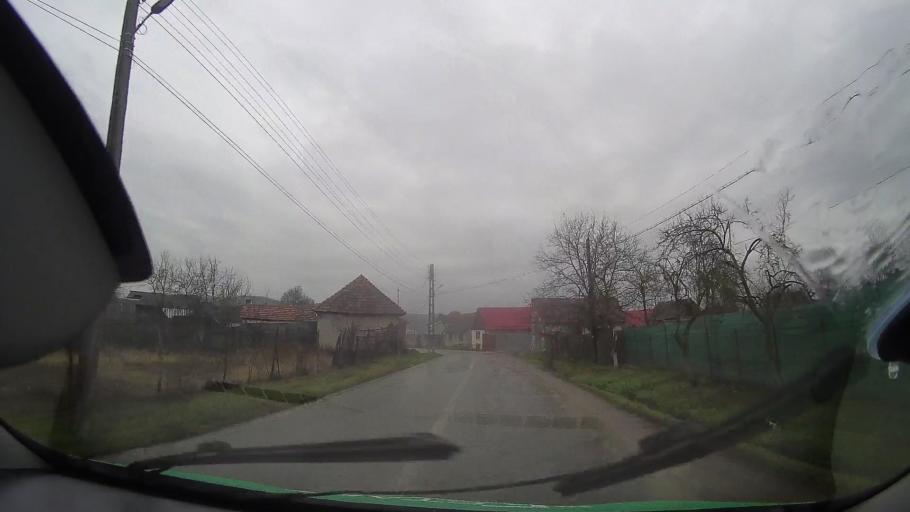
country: RO
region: Bihor
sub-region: Comuna Rabagani
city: Rabagani
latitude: 46.7470
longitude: 22.2366
